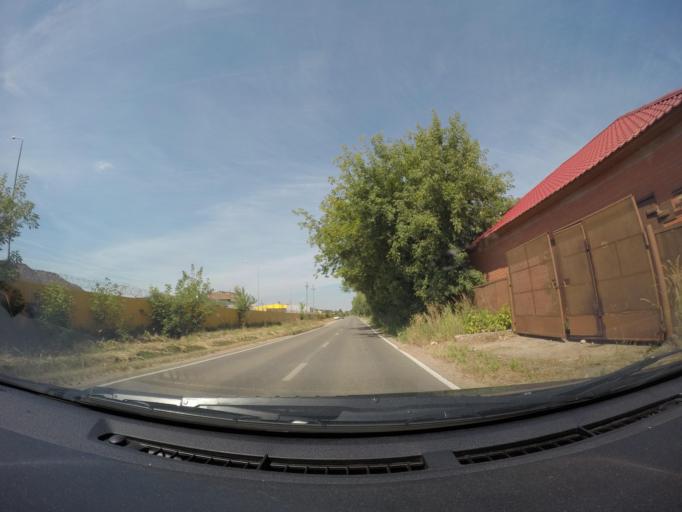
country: RU
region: Moskovskaya
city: Rechitsy
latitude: 55.6115
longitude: 38.4478
